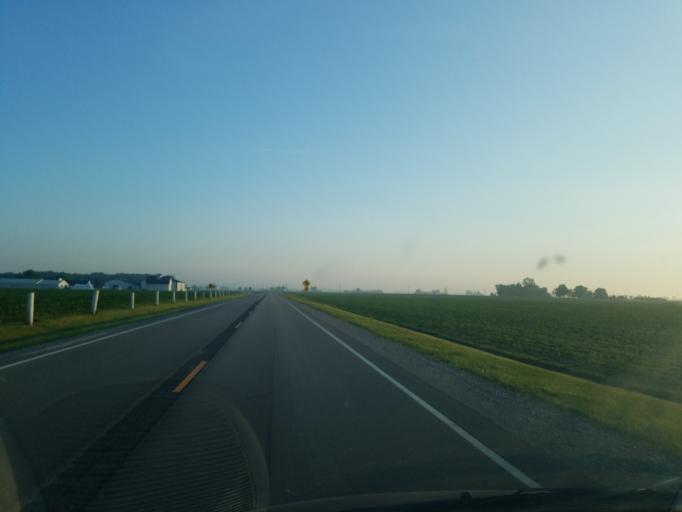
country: US
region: Indiana
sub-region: Allen County
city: Woodburn
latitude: 41.1798
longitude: -84.8493
